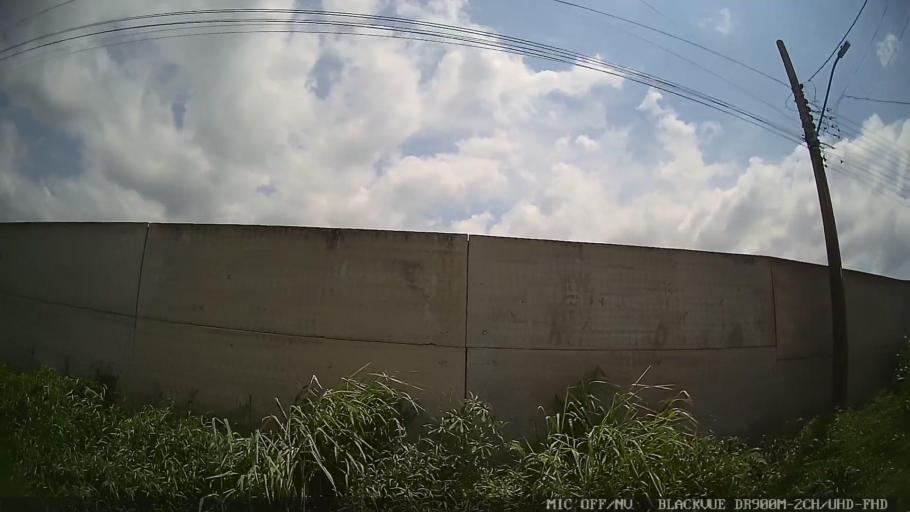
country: BR
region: Sao Paulo
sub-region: Caraguatatuba
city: Caraguatatuba
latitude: -23.6679
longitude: -45.4531
